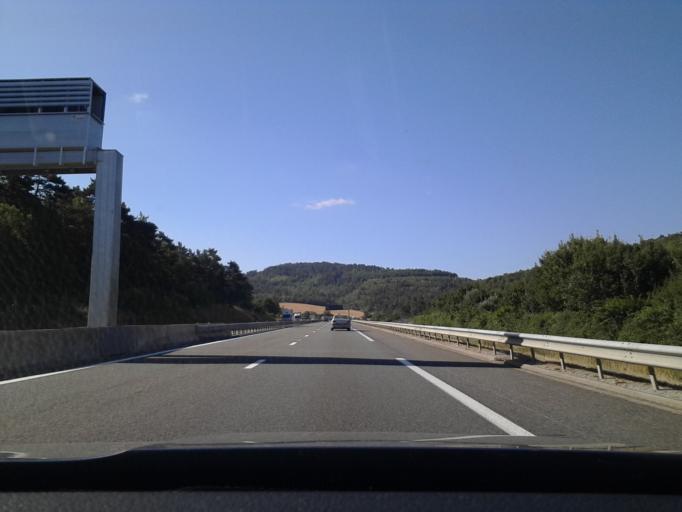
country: FR
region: Midi-Pyrenees
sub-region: Departement de l'Aveyron
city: Severac-le-Chateau
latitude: 44.3679
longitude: 3.1160
